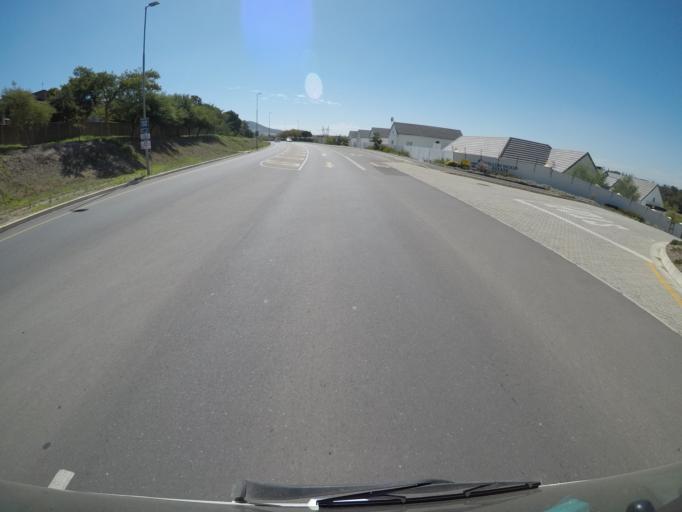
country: ZA
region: Western Cape
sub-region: City of Cape Town
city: Kraaifontein
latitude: -33.8249
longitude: 18.6371
